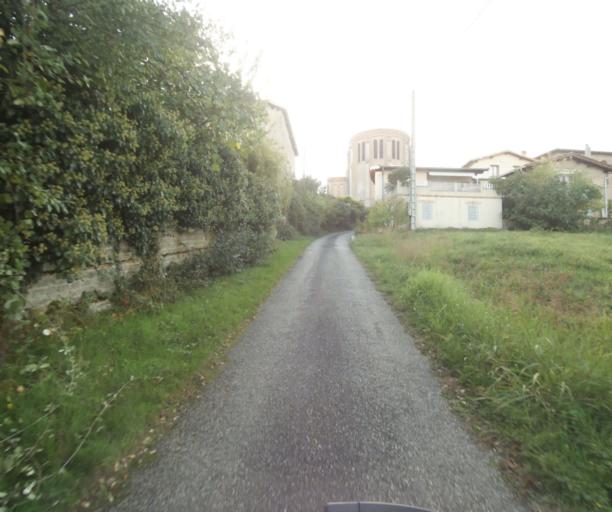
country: FR
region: Midi-Pyrenees
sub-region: Departement de la Haute-Garonne
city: Launac
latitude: 43.8212
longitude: 1.1187
